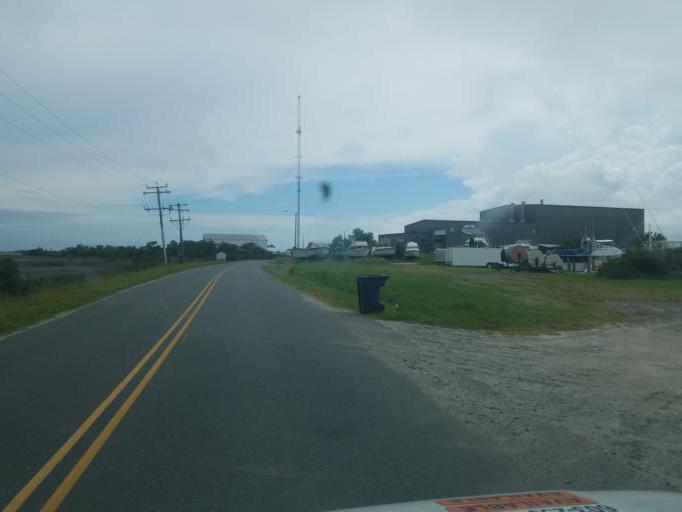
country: US
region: North Carolina
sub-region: Dare County
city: Wanchese
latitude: 35.8453
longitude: -75.6258
